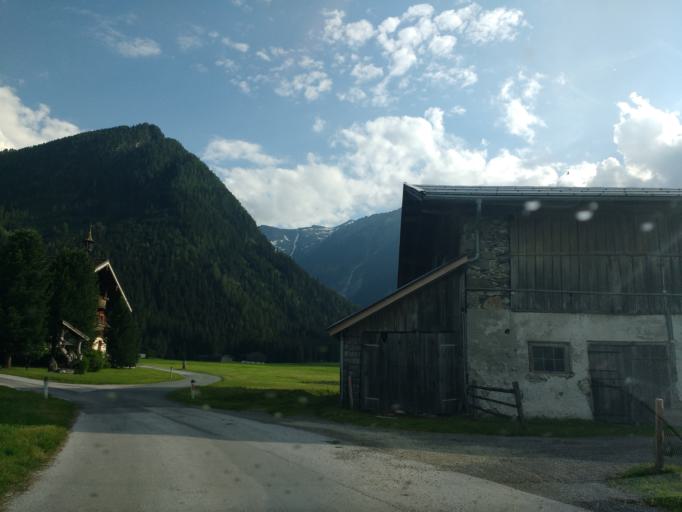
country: AT
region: Salzburg
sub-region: Politischer Bezirk Zell am See
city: Neukirchen am Grossvenediger
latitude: 47.2401
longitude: 12.2617
